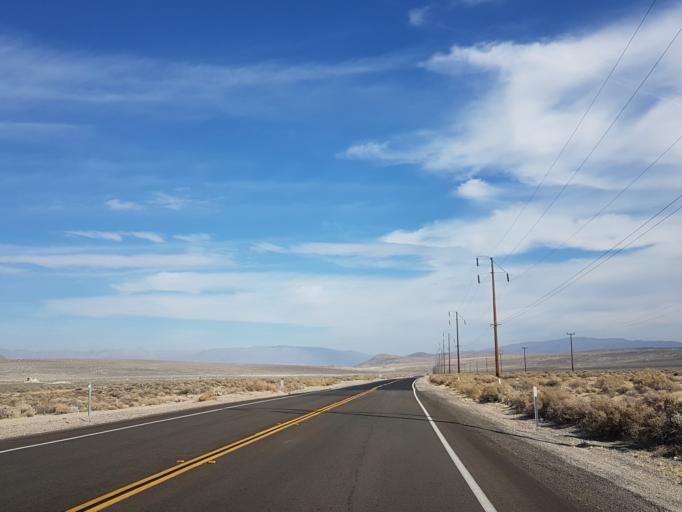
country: US
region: California
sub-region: San Bernardino County
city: Searles Valley
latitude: 35.6472
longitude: -117.5081
